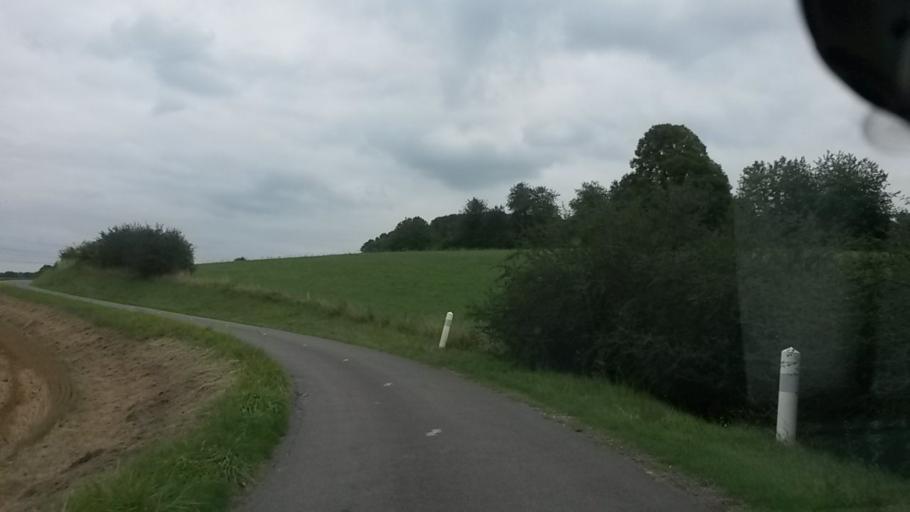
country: FR
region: Haute-Normandie
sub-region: Departement de la Seine-Maritime
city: La Feuillie
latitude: 49.4820
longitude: 1.5158
